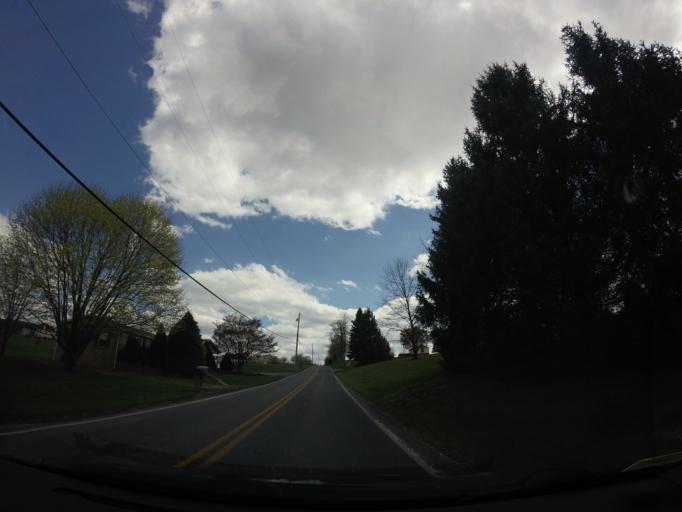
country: US
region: Maryland
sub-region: Washington County
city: Keedysville
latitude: 39.4268
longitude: -77.6728
